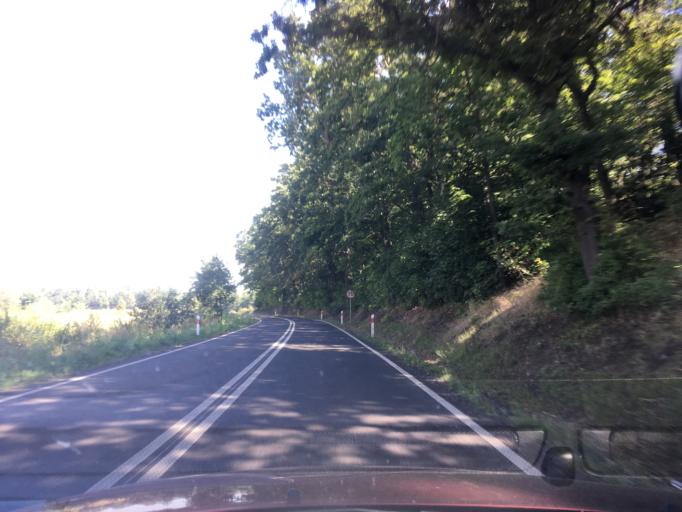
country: PL
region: Lower Silesian Voivodeship
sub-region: Powiat zgorzelecki
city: Lagow
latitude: 51.2041
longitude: 15.0209
